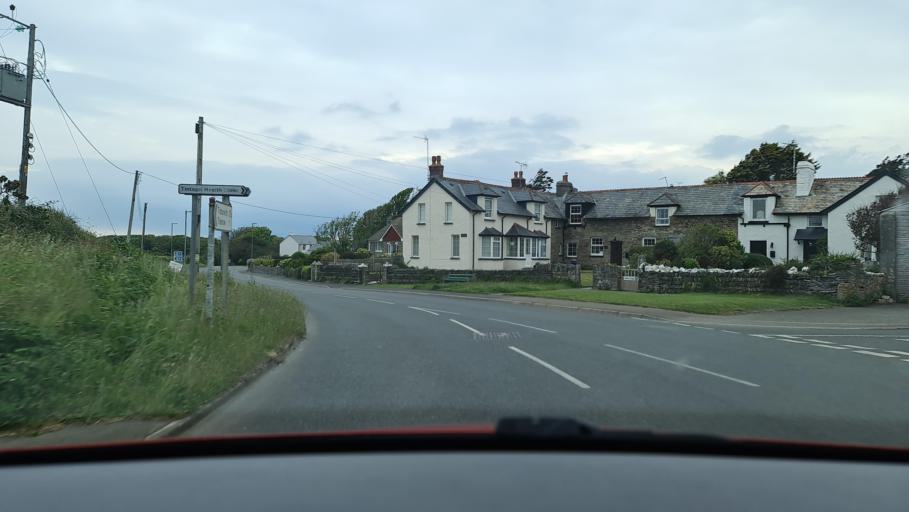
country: GB
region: England
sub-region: Cornwall
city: Tintagel
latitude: 50.6600
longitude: -4.7494
